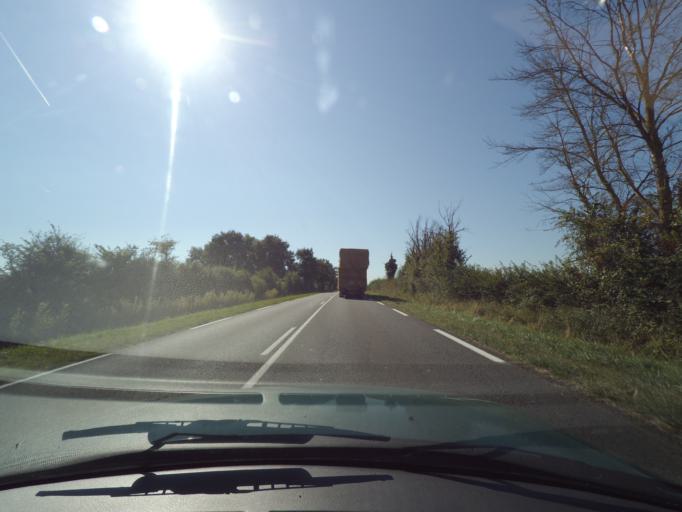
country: FR
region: Poitou-Charentes
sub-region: Departement de la Vienne
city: Lussac-les-Chateaux
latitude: 46.3802
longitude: 0.7518
